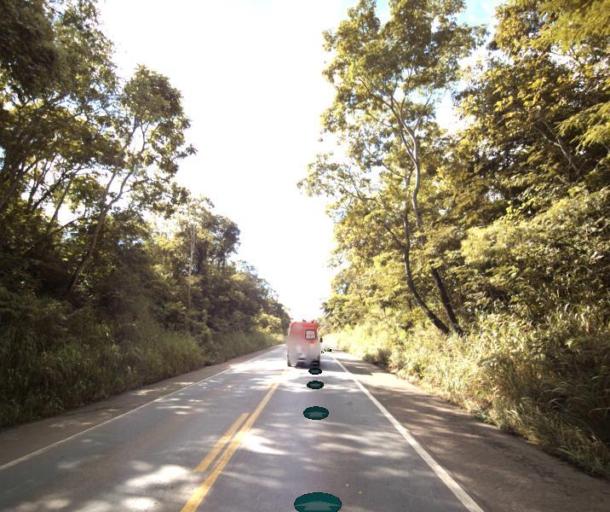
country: BR
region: Goias
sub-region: Jaragua
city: Jaragua
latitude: -15.6034
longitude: -49.4055
